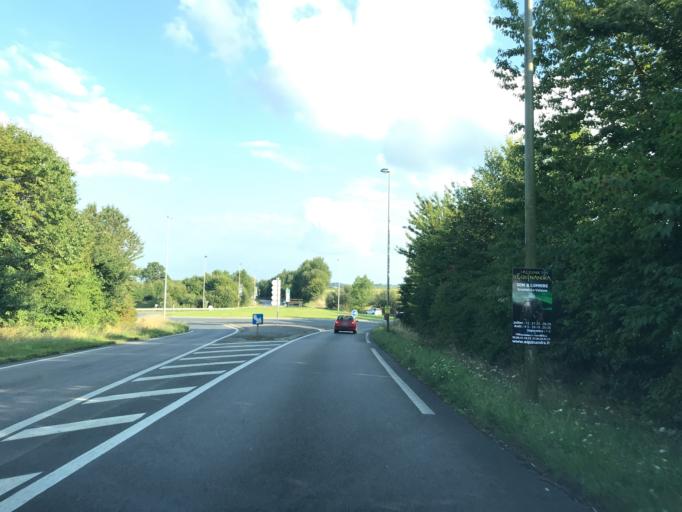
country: FR
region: Haute-Normandie
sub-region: Departement de la Seine-Maritime
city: Bolbec
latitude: 49.5749
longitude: 0.4563
